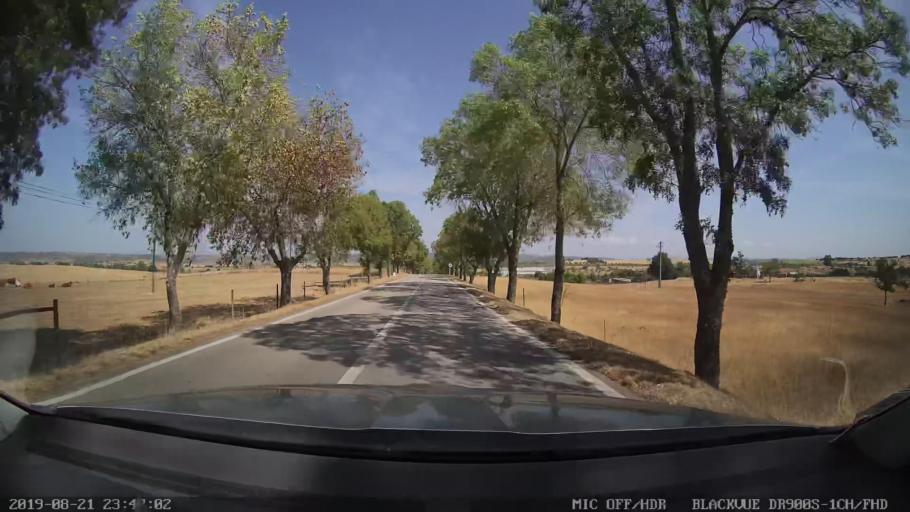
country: PT
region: Castelo Branco
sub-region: Idanha-A-Nova
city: Idanha-a-Nova
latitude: 39.8467
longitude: -7.2570
